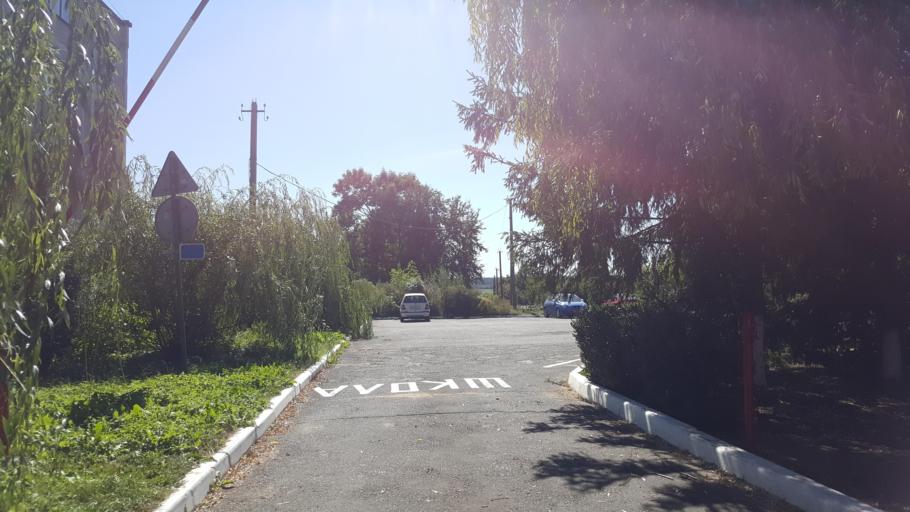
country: BY
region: Brest
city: Vysokaye
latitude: 52.2220
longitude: 23.4537
